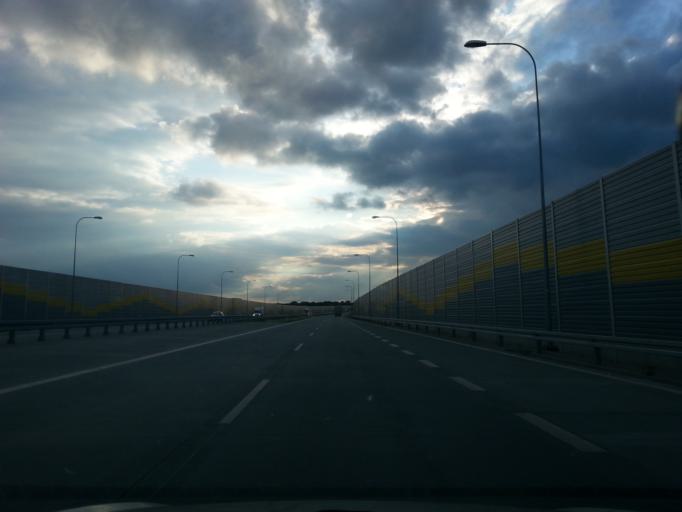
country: PL
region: Lodz Voivodeship
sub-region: Powiat zdunskowolski
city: Zdunska Wola
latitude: 51.5761
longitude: 18.9304
